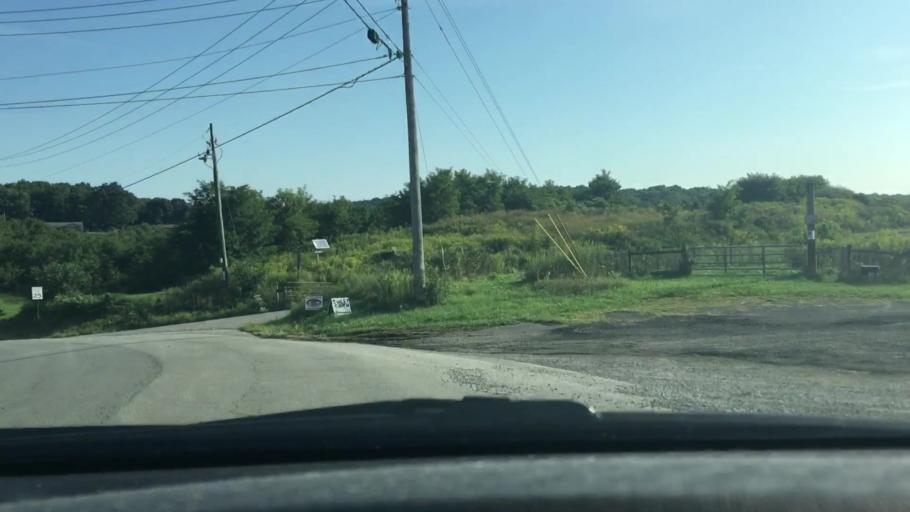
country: US
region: Pennsylvania
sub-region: Butler County
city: Zelienople
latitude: 40.7708
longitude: -80.1062
